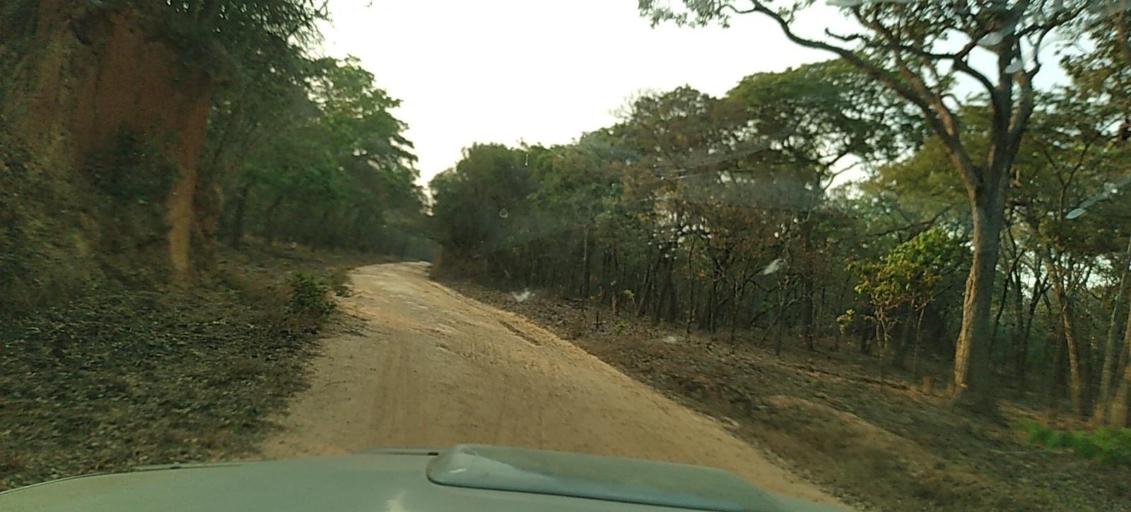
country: ZM
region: North-Western
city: Kasempa
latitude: -13.1601
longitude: 26.4504
